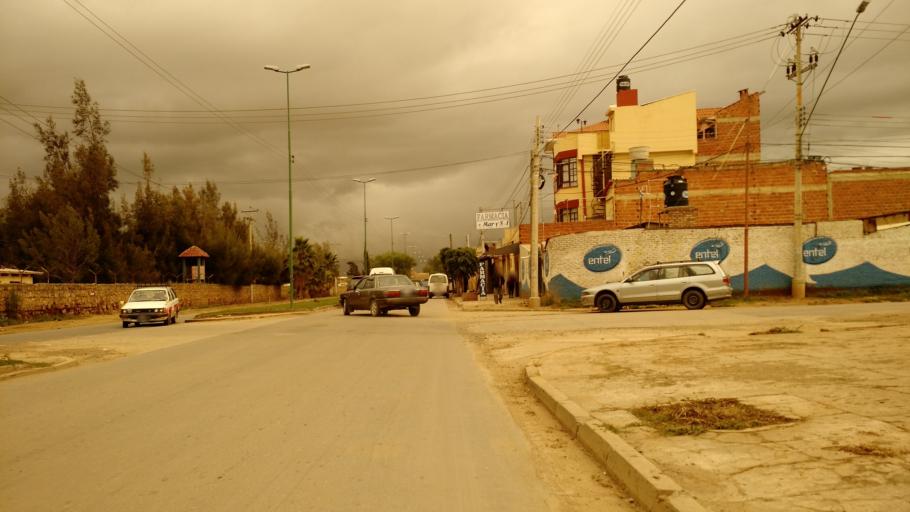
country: BO
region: Cochabamba
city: Cochabamba
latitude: -17.4263
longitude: -66.1661
